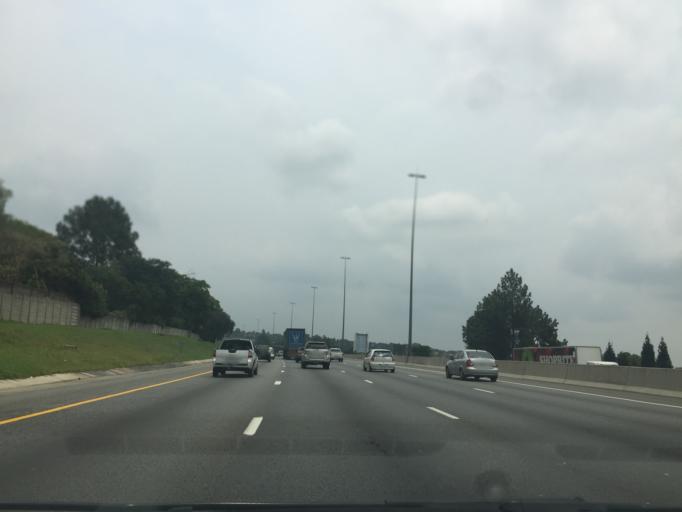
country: ZA
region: Gauteng
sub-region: City of Johannesburg Metropolitan Municipality
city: Midrand
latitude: -26.0344
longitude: 28.0358
